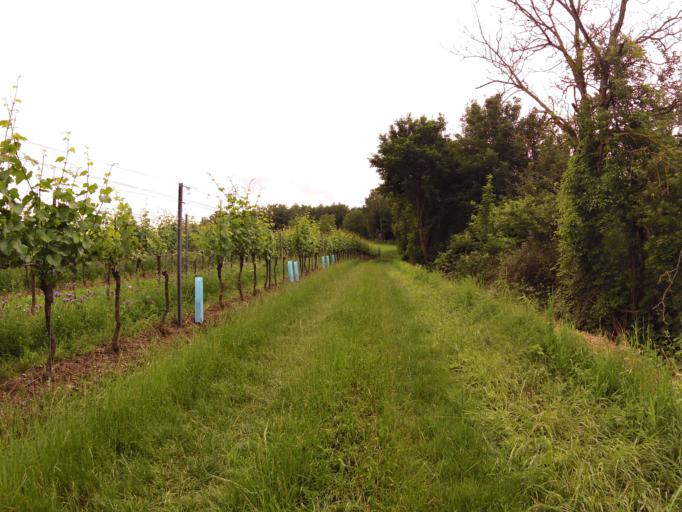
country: DE
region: Baden-Wuerttemberg
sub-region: Freiburg Region
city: Lahr
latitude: 48.3549
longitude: 7.8606
